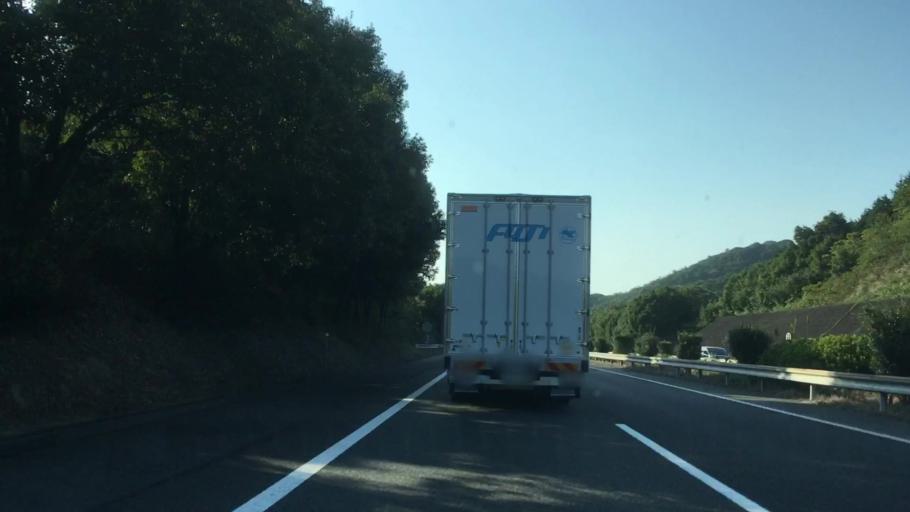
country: JP
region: Yamaguchi
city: Ogori-shimogo
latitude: 34.0845
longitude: 131.4732
